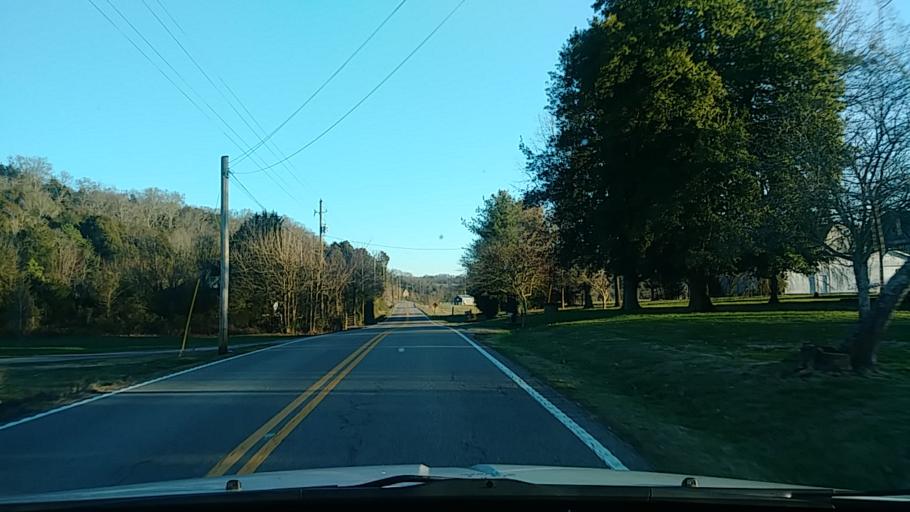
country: US
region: Tennessee
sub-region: Jefferson County
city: White Pine
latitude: 36.1296
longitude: -83.1273
